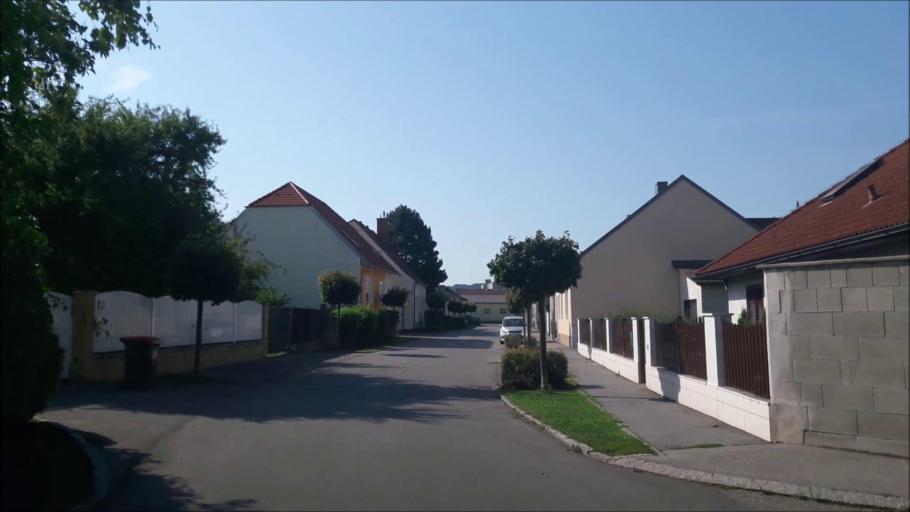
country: AT
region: Lower Austria
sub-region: Politischer Bezirk Bruck an der Leitha
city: Bruck an der Leitha
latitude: 48.0248
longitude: 16.7733
